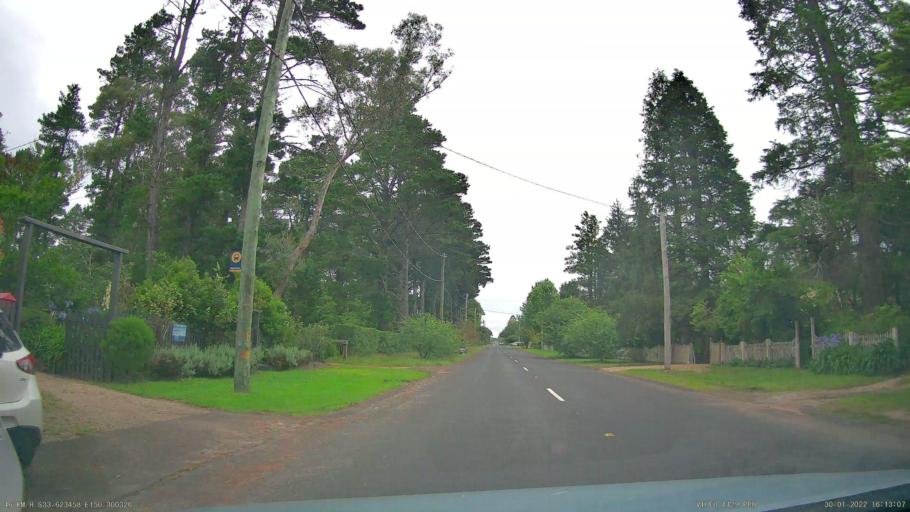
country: AU
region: New South Wales
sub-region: Blue Mountains Municipality
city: Blackheath
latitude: -33.6235
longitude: 150.3002
